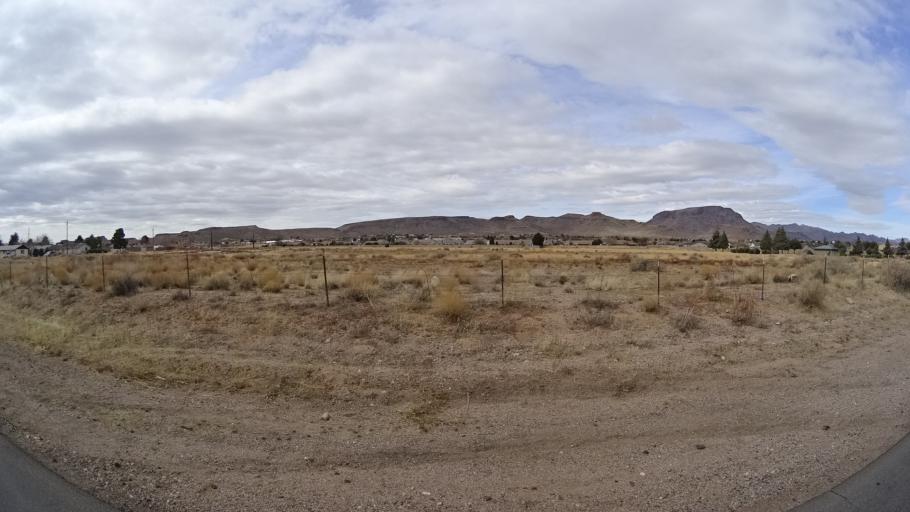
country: US
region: Arizona
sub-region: Mohave County
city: New Kingman-Butler
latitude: 35.2328
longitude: -114.0252
